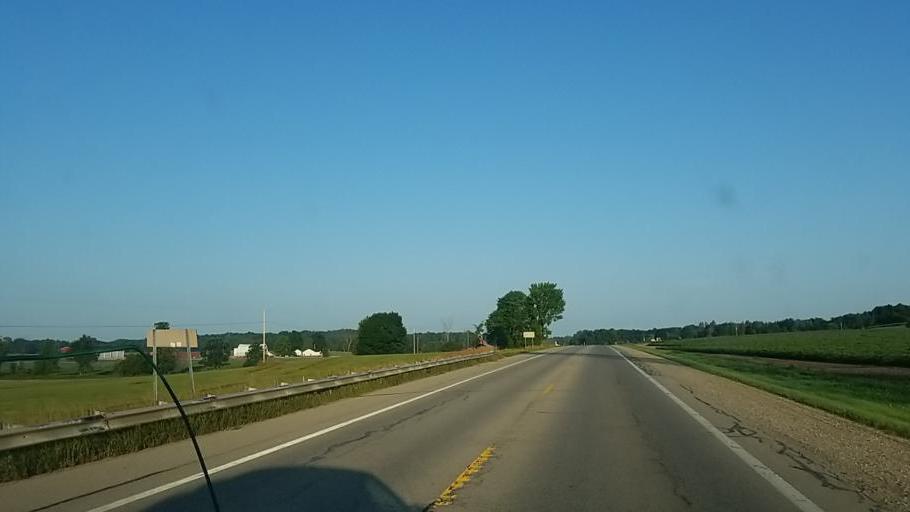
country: US
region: Michigan
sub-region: Montcalm County
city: Lakeview
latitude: 43.4304
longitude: -85.2062
